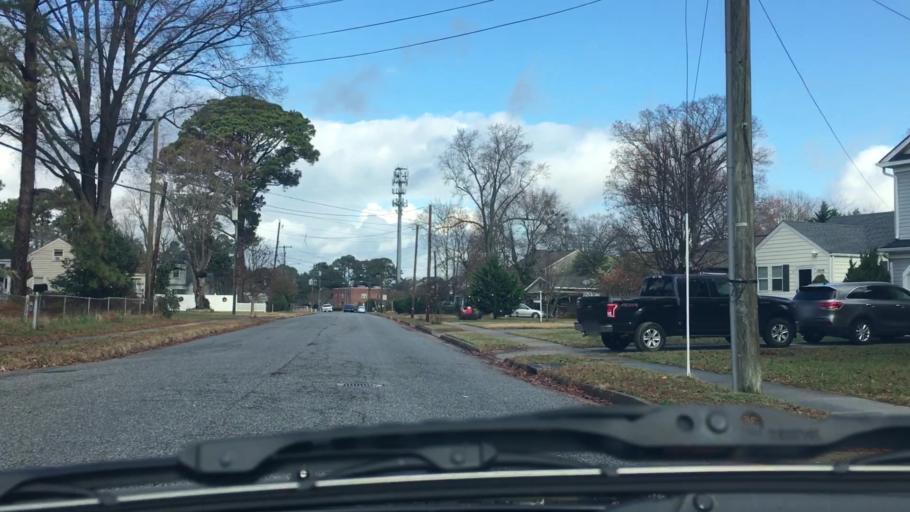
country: US
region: Virginia
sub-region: City of Norfolk
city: Norfolk
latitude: 36.9267
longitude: -76.2455
